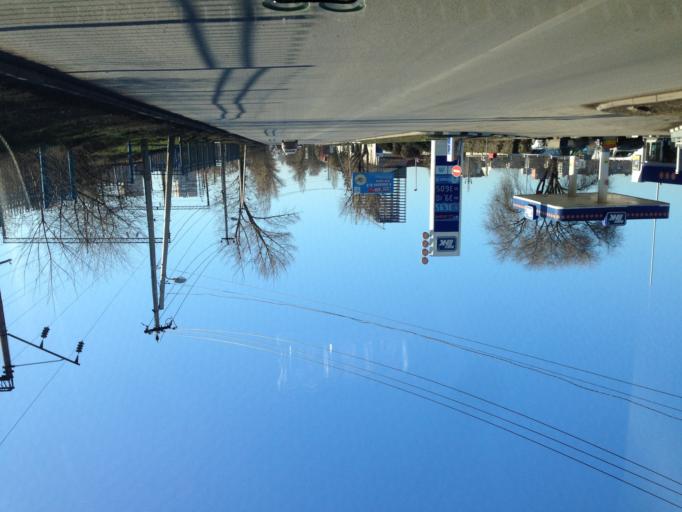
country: RU
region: Rostov
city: Rostov-na-Donu
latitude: 47.2458
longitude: 39.6862
